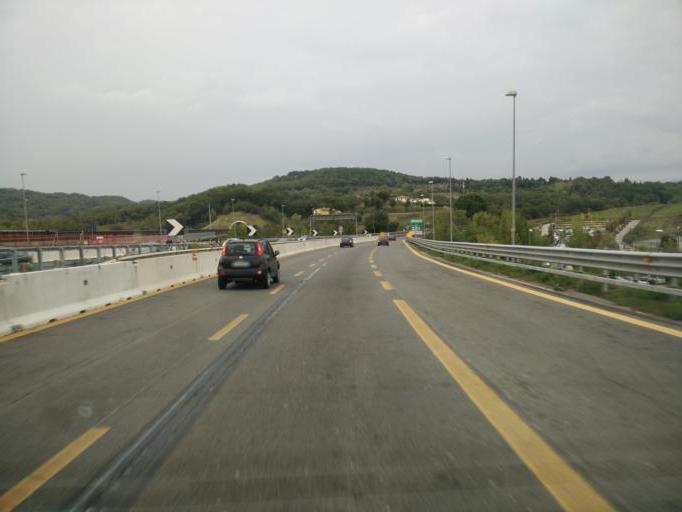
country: IT
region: Tuscany
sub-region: Province of Florence
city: Cavallina
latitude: 43.9856
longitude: 11.2114
